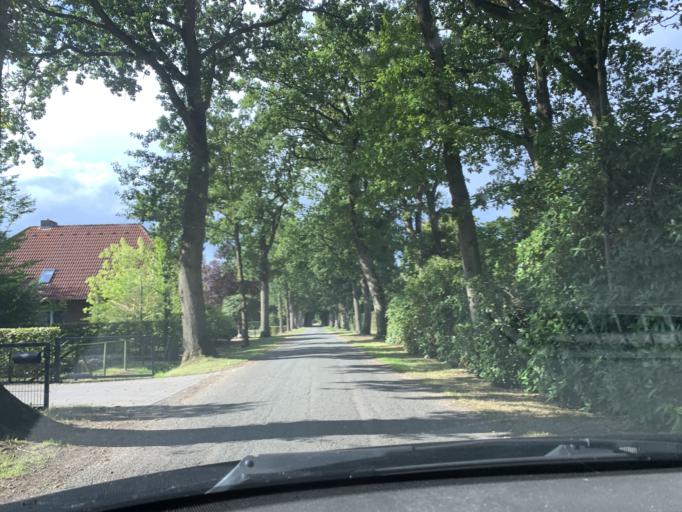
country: DE
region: Lower Saxony
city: Bad Zwischenahn
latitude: 53.2324
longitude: 7.9952
